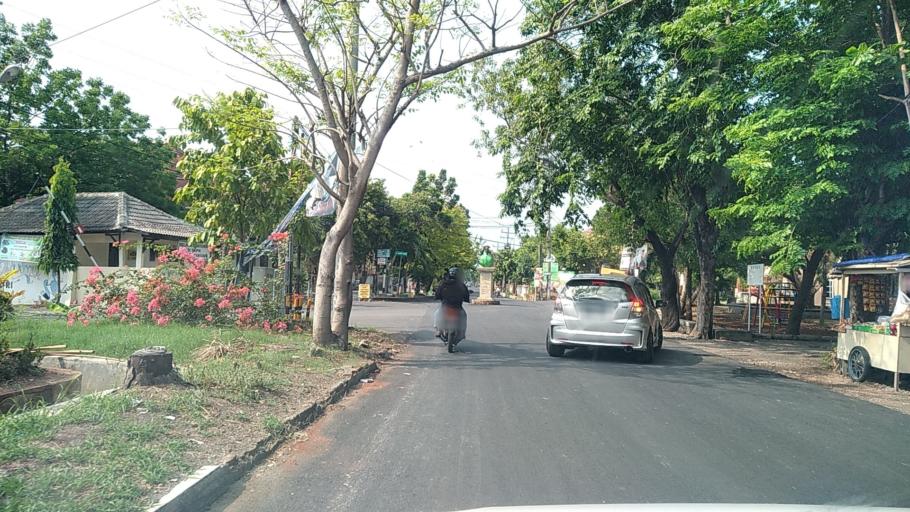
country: ID
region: Central Java
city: Semarang
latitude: -7.0011
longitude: 110.4490
